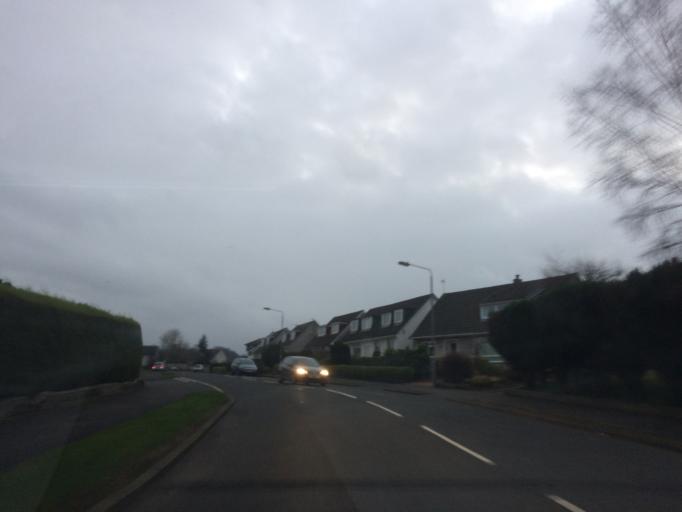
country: GB
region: Scotland
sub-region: East Renfrewshire
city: Newton Mearns
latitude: 55.7836
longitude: -4.3340
